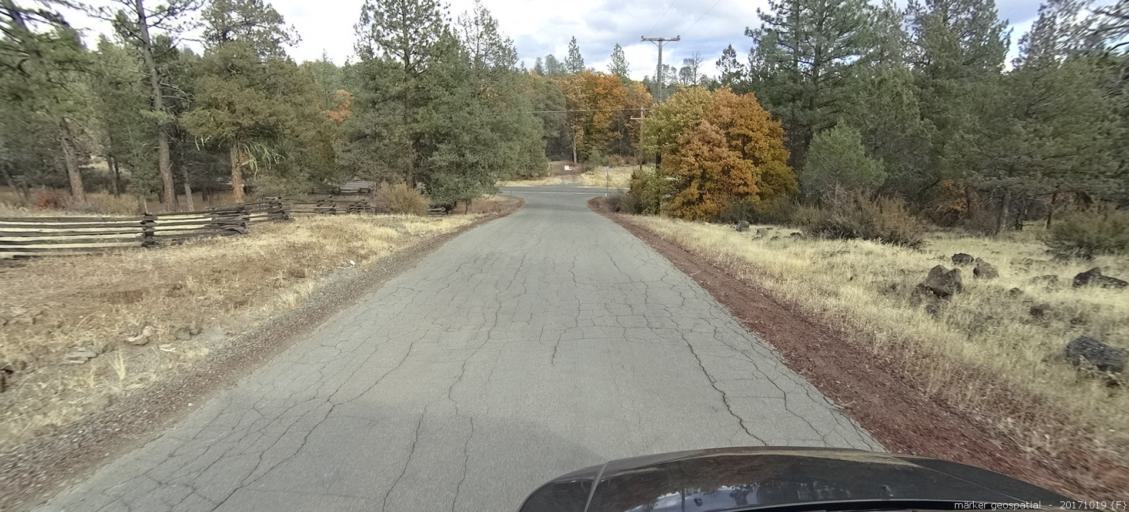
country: US
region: California
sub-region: Shasta County
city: Burney
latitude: 40.9781
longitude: -121.4342
